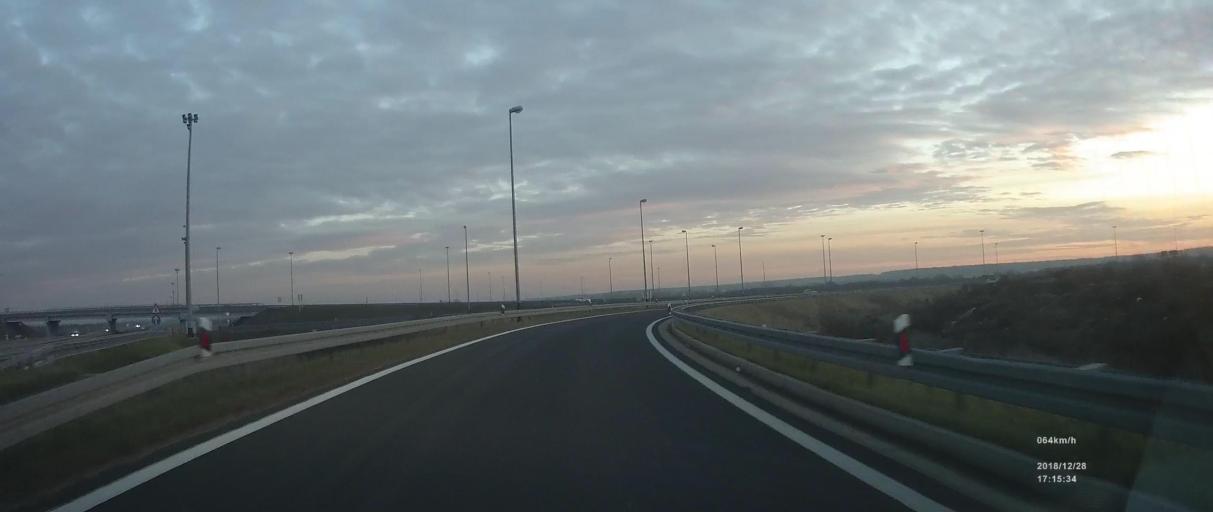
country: HR
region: Zagrebacka
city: Gradici
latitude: 45.6923
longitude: 16.0638
